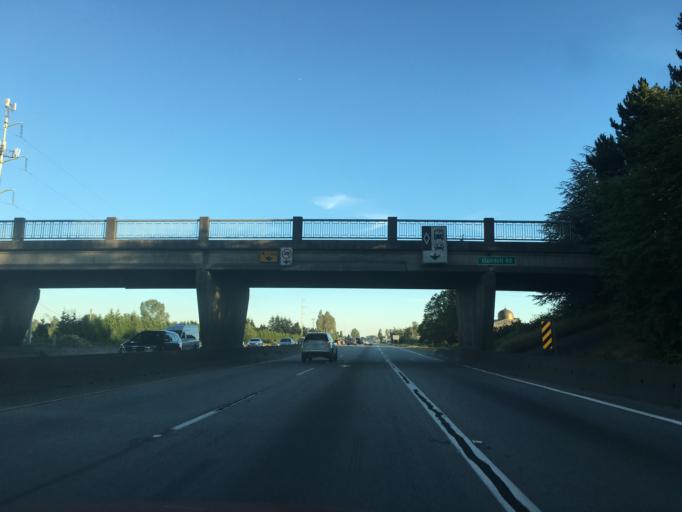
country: CA
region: British Columbia
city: Richmond
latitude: 49.1562
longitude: -123.0868
